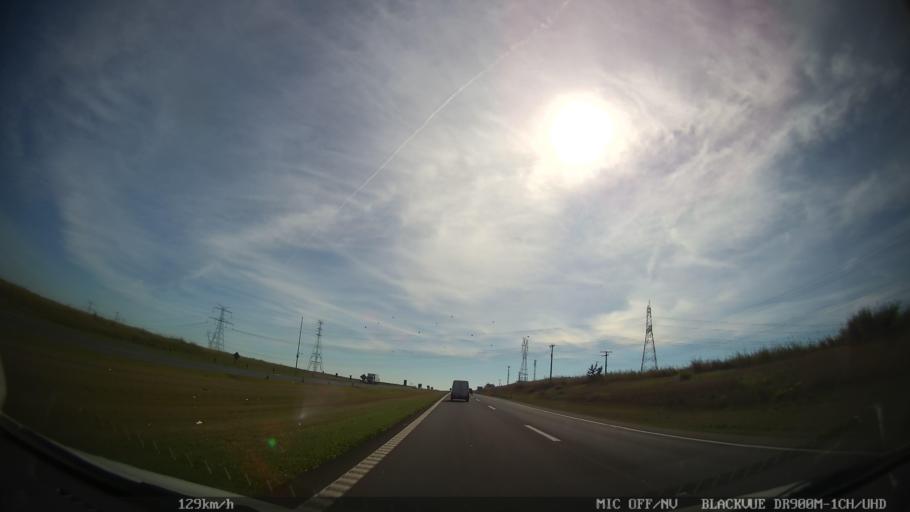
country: BR
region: Sao Paulo
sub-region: Cordeiropolis
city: Cordeiropolis
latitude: -22.4435
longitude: -47.3979
